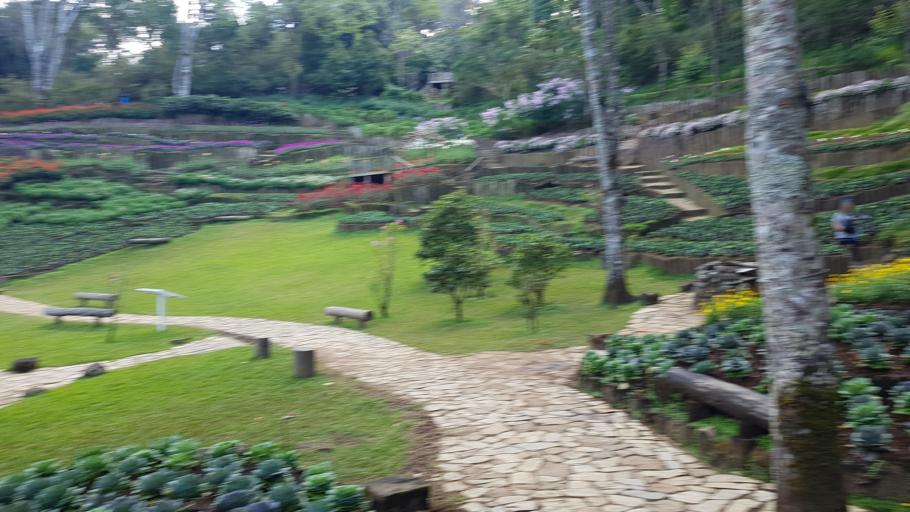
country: TH
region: Chiang Rai
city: Mae Fa Luang
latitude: 20.3355
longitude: 99.8118
